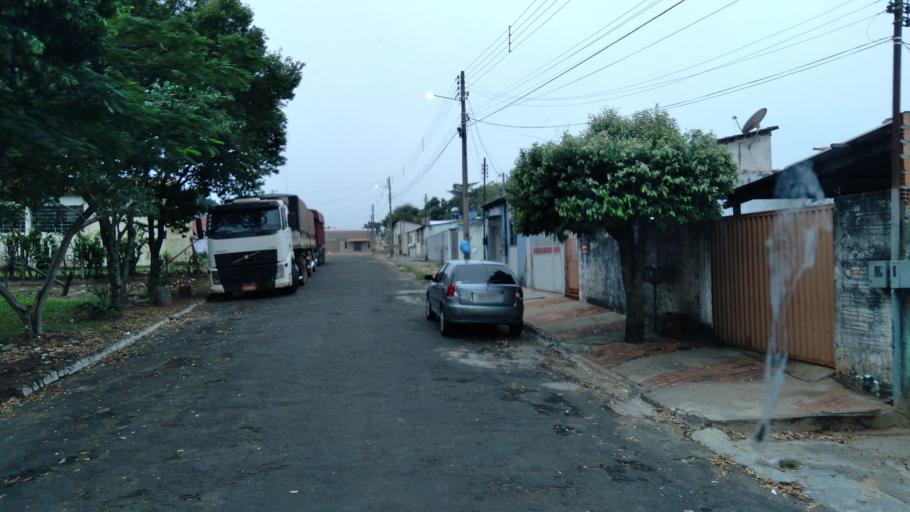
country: BR
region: Goias
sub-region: Mineiros
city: Mineiros
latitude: -17.5751
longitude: -52.5413
